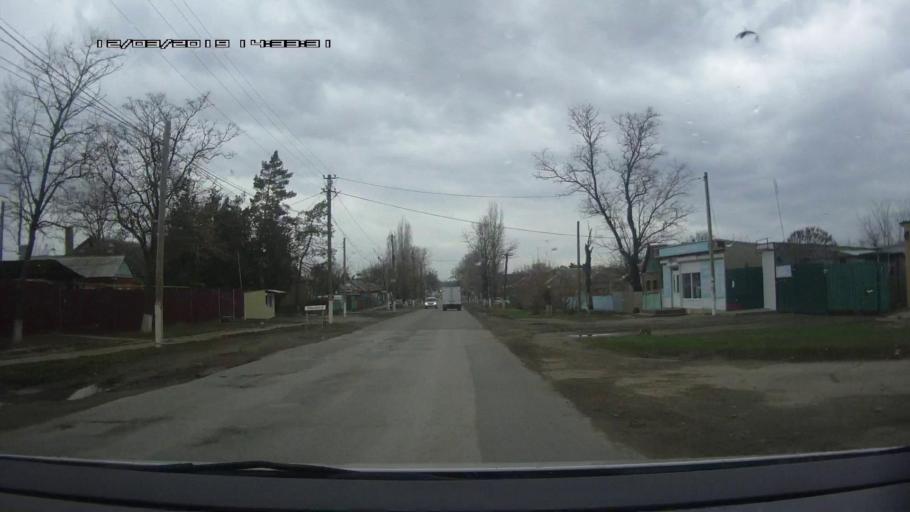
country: RU
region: Rostov
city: Novobataysk
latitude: 46.8986
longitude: 39.7804
